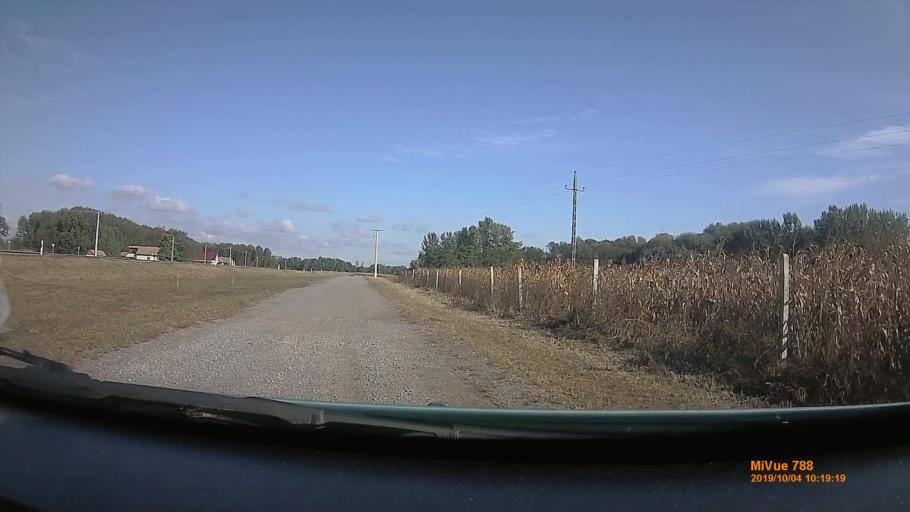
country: HU
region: Szabolcs-Szatmar-Bereg
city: Nyiregyhaza
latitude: 47.9611
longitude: 21.6569
